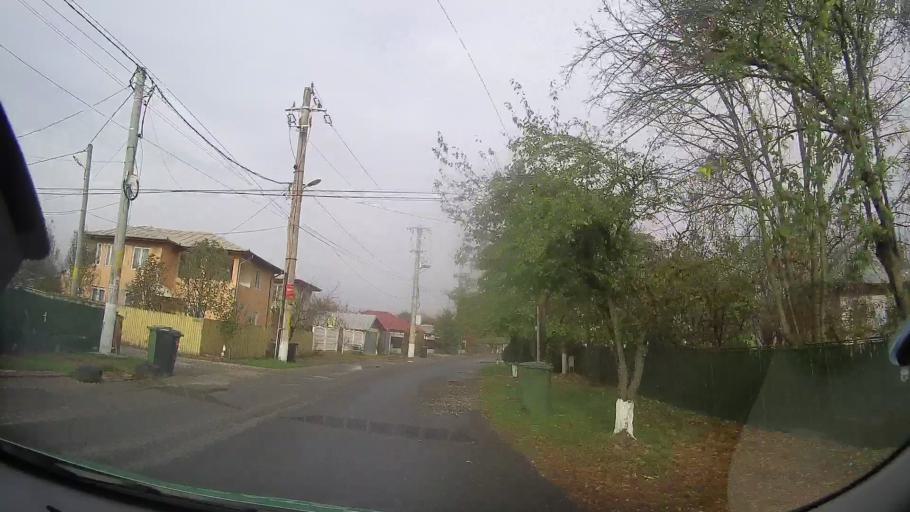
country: RO
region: Ilfov
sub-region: Comuna Snagov
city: Snagov
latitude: 44.7131
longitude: 26.1738
